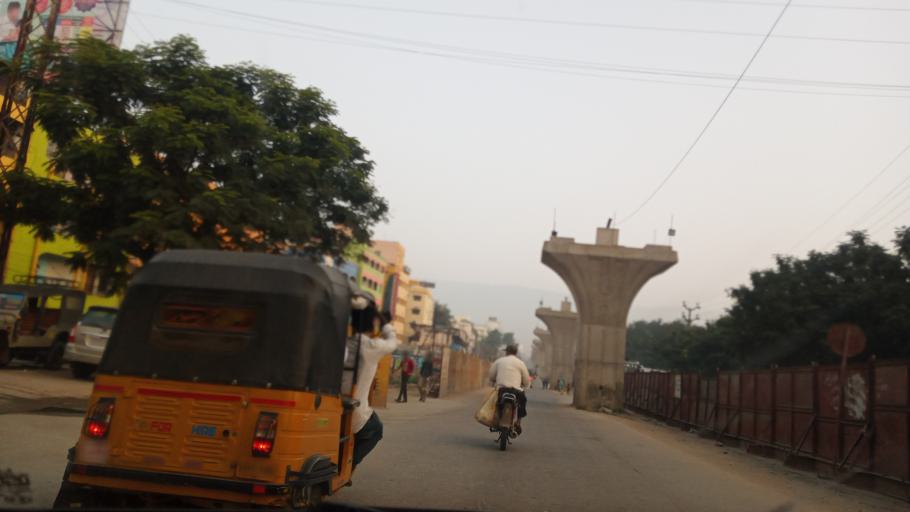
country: IN
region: Andhra Pradesh
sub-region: Chittoor
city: Tirupati
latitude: 13.6312
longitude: 79.4280
